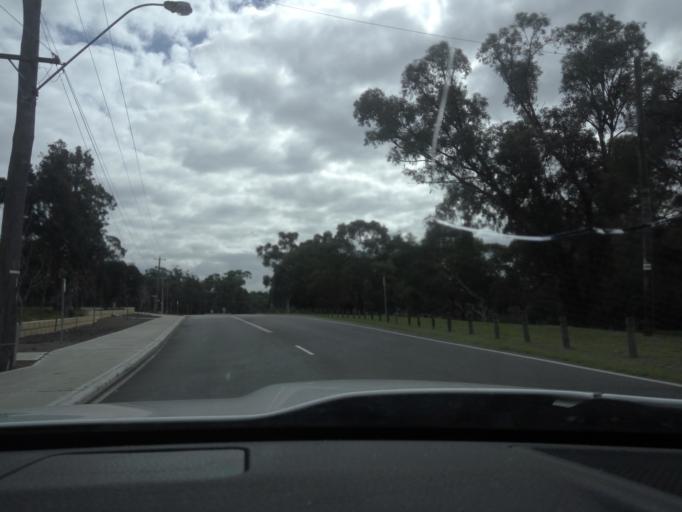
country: AU
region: Western Australia
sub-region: City of Cockburn
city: Bibra Lake
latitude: -32.0923
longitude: 115.8205
